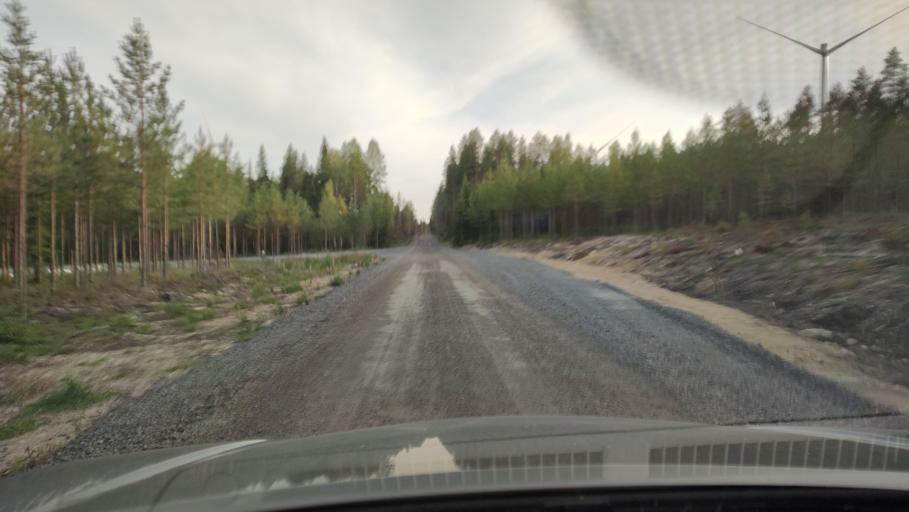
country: FI
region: Southern Ostrobothnia
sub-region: Suupohja
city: Karijoki
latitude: 62.1543
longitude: 21.6175
